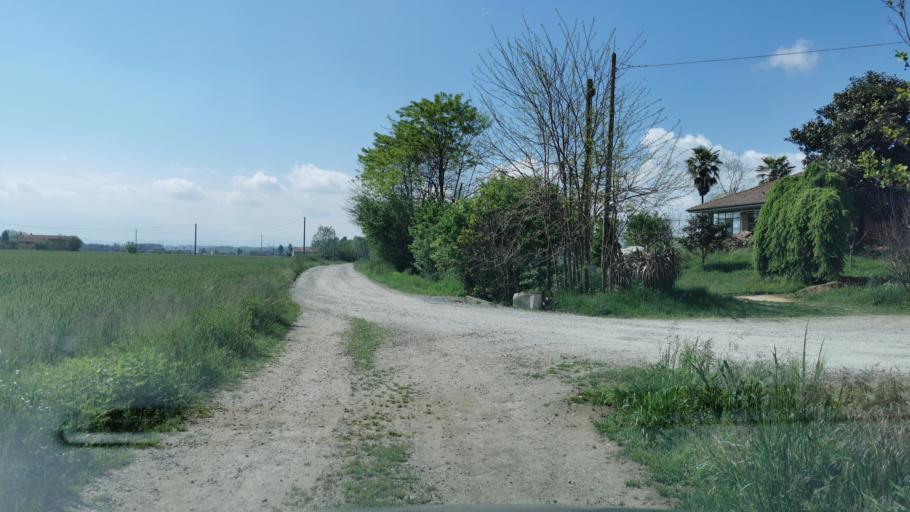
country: IT
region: Piedmont
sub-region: Provincia di Torino
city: Feletto
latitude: 45.2817
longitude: 7.7224
